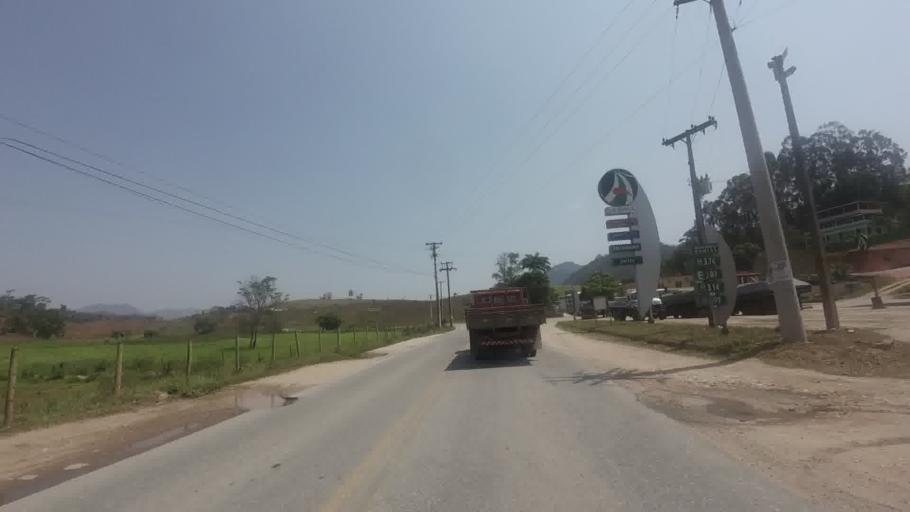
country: BR
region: Espirito Santo
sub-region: Cachoeiro De Itapemirim
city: Cachoeiro de Itapemirim
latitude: -20.8689
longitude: -41.0258
